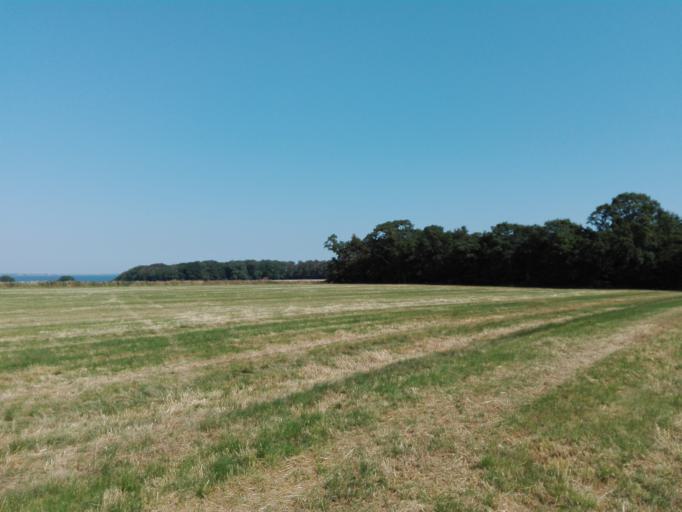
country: DK
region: Central Jutland
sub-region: Hedensted Kommune
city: Juelsminde
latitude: 55.7476
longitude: 10.0465
